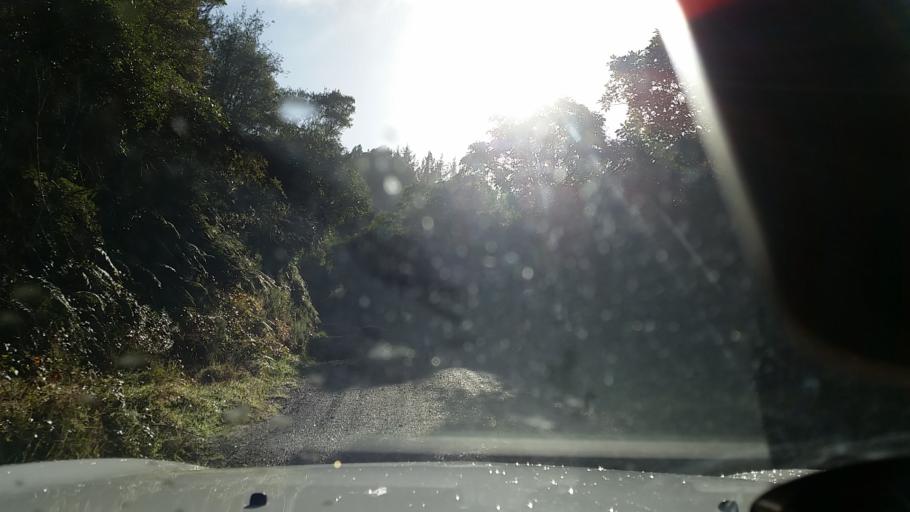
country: NZ
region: Bay of Plenty
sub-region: Kawerau District
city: Kawerau
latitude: -38.0087
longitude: 176.5983
